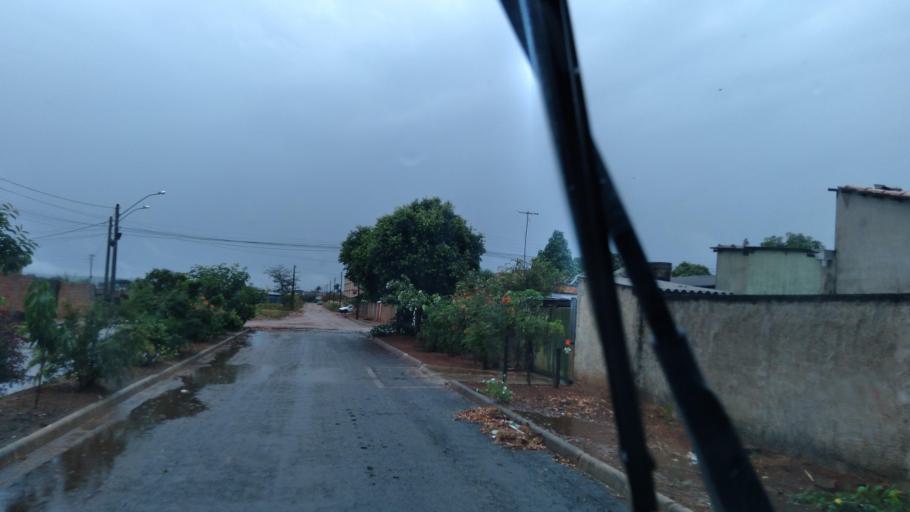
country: BR
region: Goias
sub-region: Mineiros
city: Mineiros
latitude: -17.5397
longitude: -52.5452
